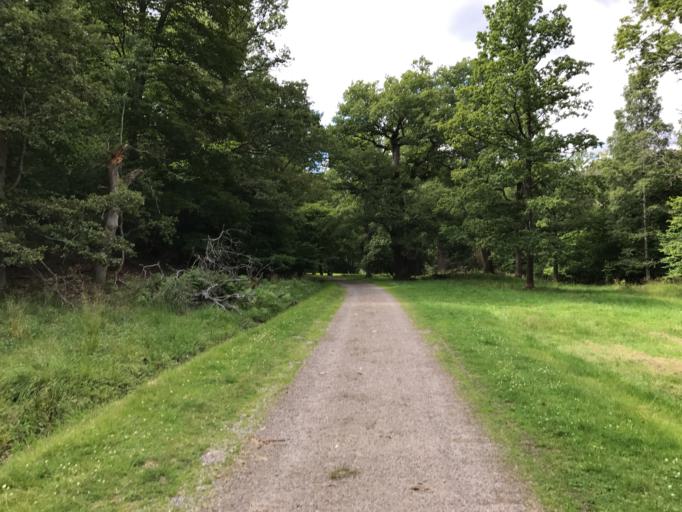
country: SE
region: Stockholm
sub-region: Lidingo
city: Lidingoe
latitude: 59.3286
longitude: 18.1263
